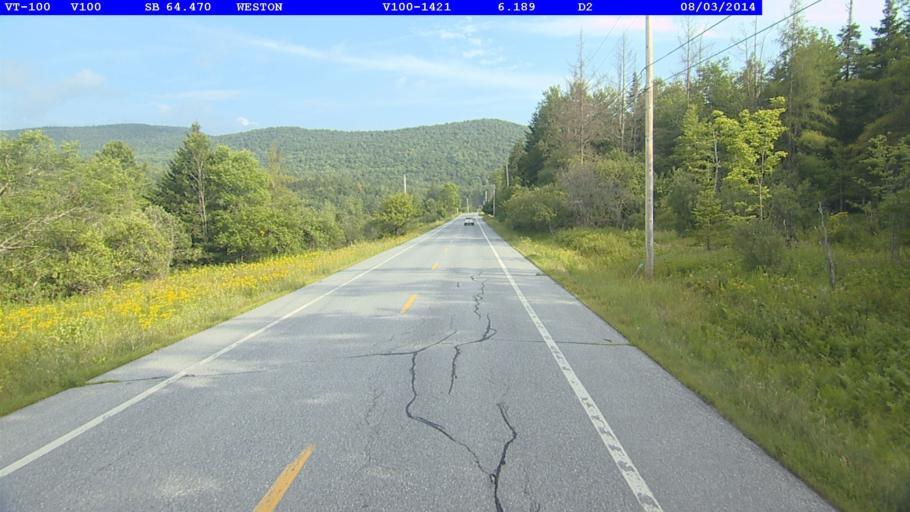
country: US
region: Vermont
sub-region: Windsor County
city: Chester
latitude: 43.3319
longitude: -72.7832
